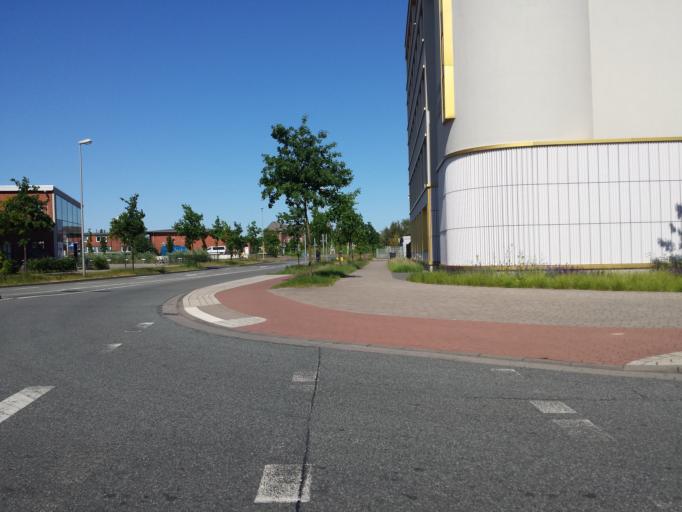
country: DE
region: Bremen
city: Bremen
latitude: 53.0946
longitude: 8.7722
